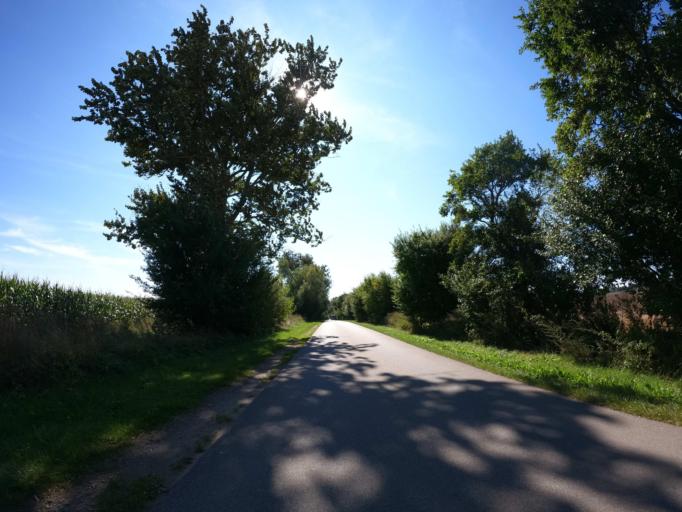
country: DE
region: Mecklenburg-Vorpommern
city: Prohn
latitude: 54.3825
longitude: 13.0251
